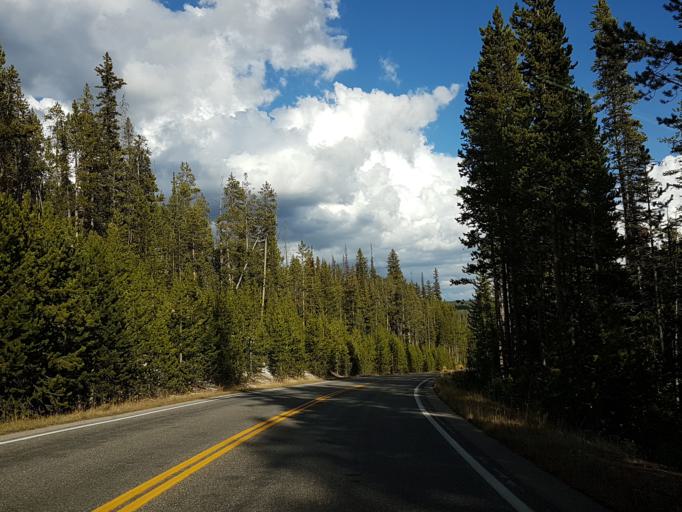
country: US
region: Montana
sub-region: Gallatin County
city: West Yellowstone
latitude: 44.4474
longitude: -110.7123
